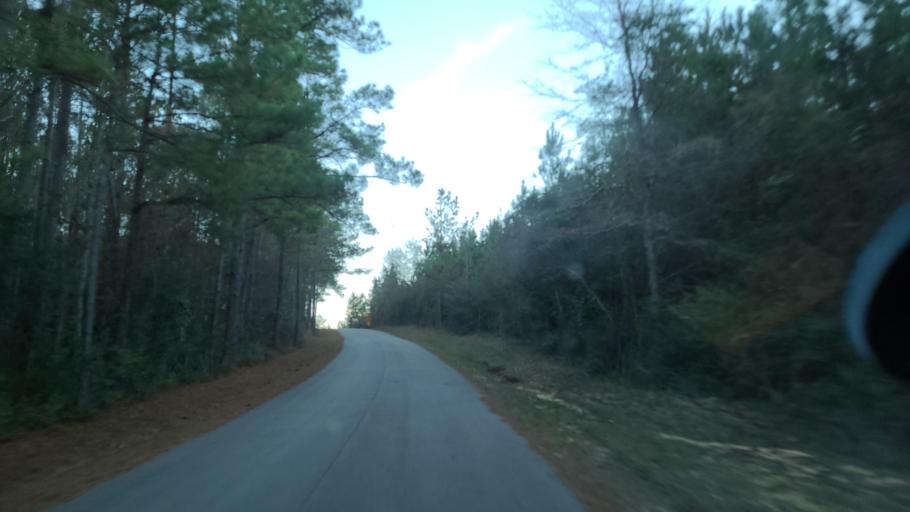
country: US
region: Mississippi
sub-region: Perry County
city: New Augusta
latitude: 31.1328
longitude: -89.2049
